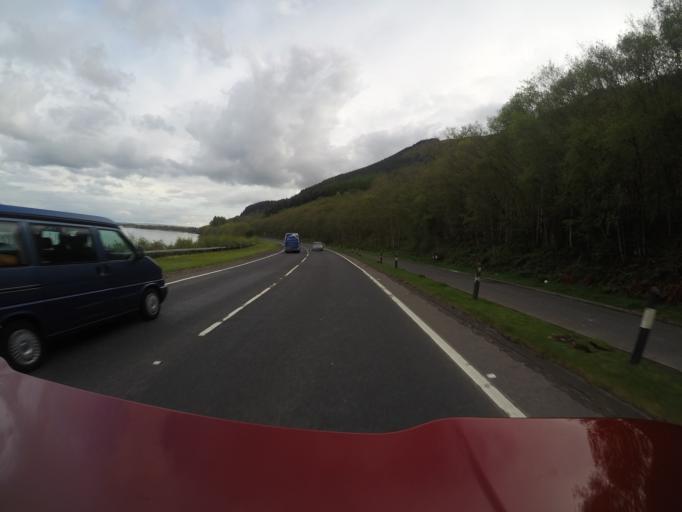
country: GB
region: Scotland
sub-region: Argyll and Bute
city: Helensburgh
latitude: 56.1583
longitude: -4.6715
